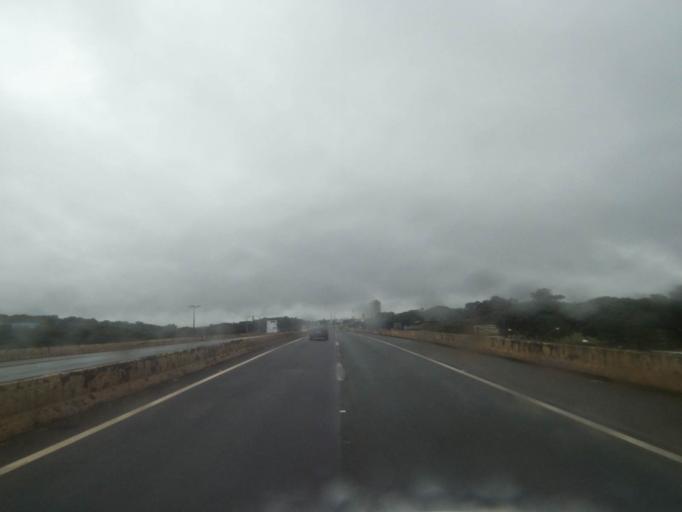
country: PY
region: Alto Parana
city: Ciudad del Este
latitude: -25.5071
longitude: -54.5853
